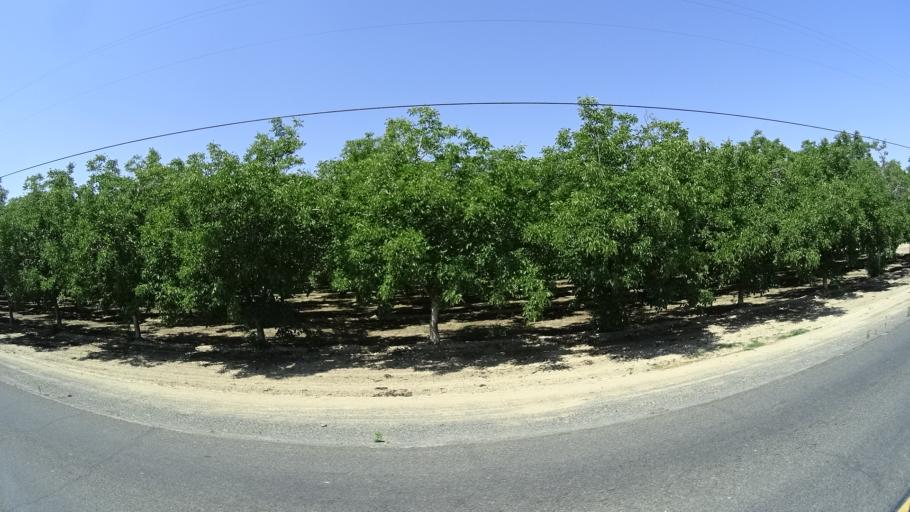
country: US
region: California
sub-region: Fresno County
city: Laton
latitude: 36.4151
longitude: -119.6728
